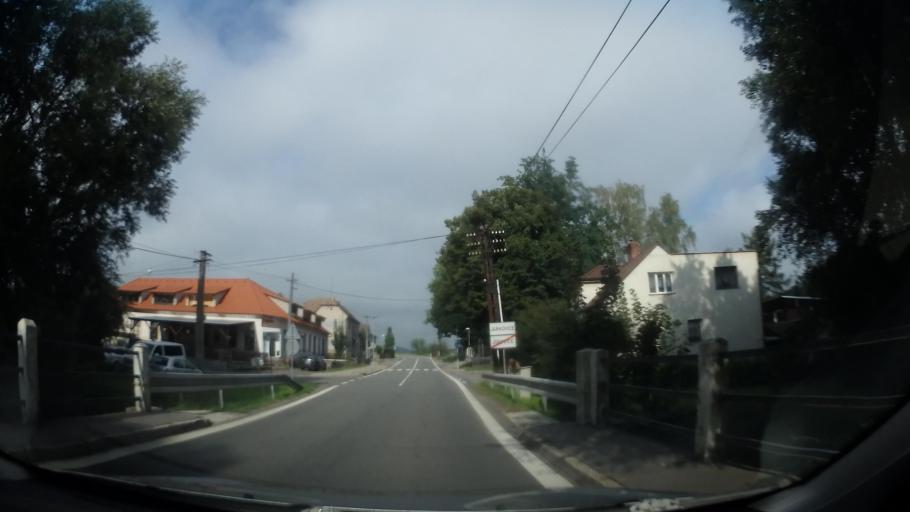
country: CZ
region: Central Bohemia
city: Bystrice
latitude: 49.7584
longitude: 14.6614
